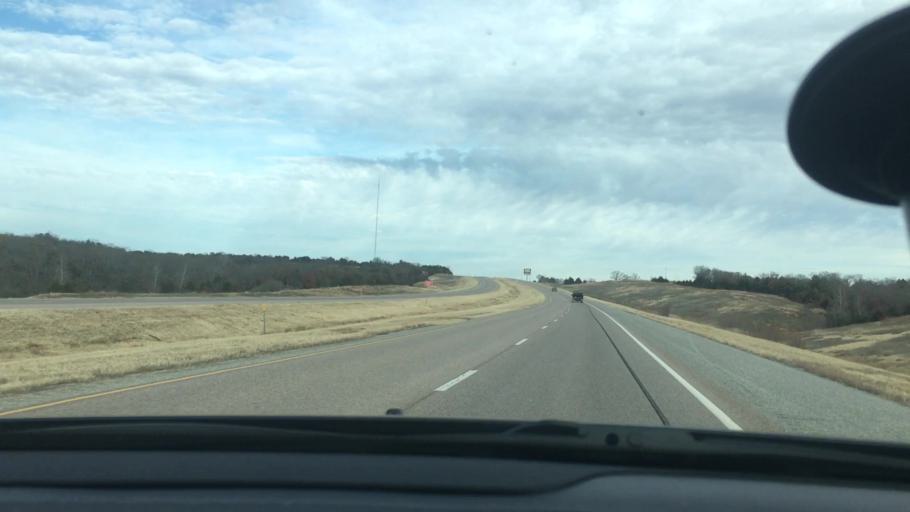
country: US
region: Oklahoma
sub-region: Pontotoc County
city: Byng
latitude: 34.8837
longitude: -96.6757
